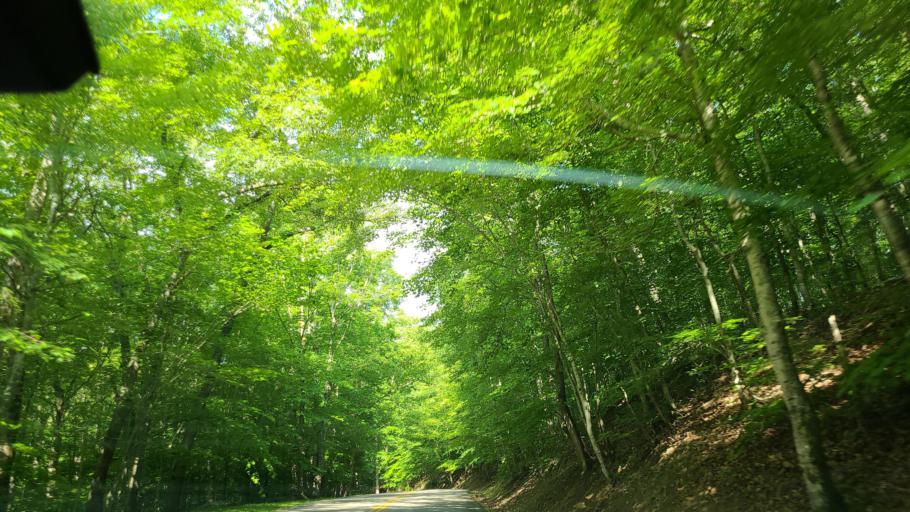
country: US
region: Kentucky
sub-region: Bell County
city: Pineville
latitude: 36.7409
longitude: -83.7058
